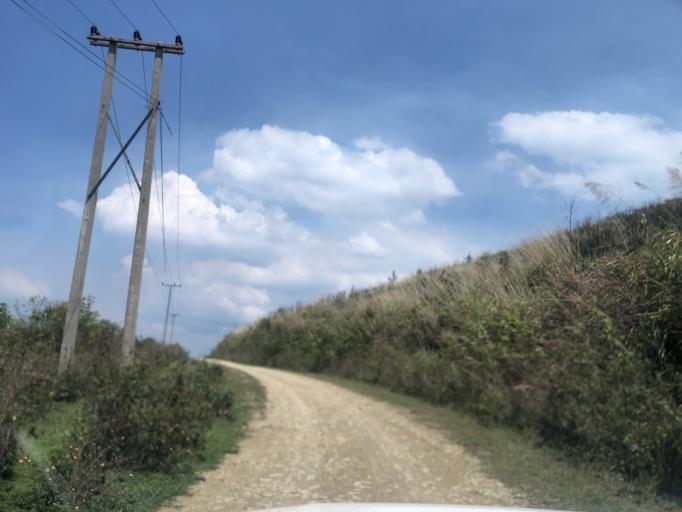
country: LA
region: Phongsali
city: Phongsali
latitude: 21.4026
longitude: 102.1873
